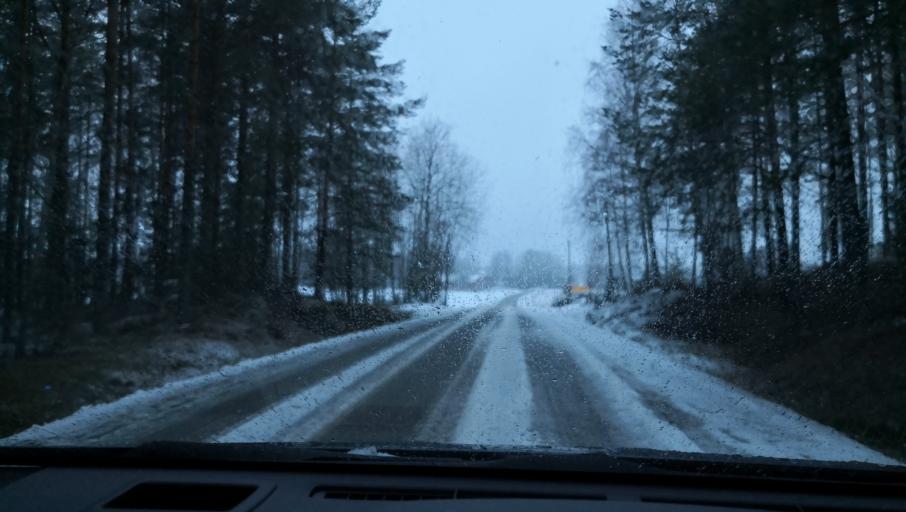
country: SE
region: Vaestmanland
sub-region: Kopings Kommun
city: Koping
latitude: 59.5752
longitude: 15.9534
